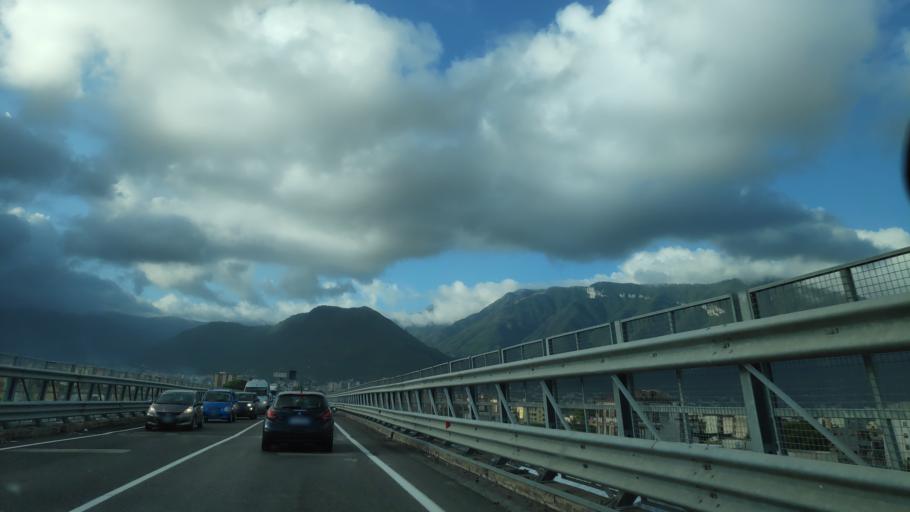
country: IT
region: Campania
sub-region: Provincia di Napoli
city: Castellammare di Stabia
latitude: 40.7168
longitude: 14.4946
